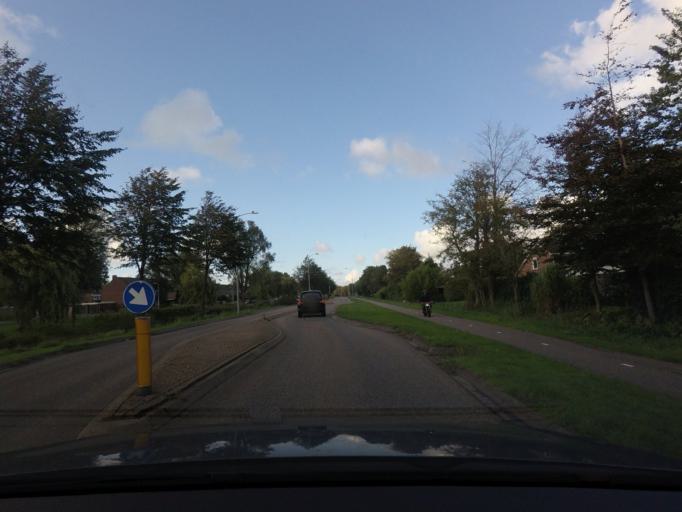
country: NL
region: North Holland
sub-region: Gemeente Uitgeest
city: Uitgeest
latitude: 52.5602
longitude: 4.7329
